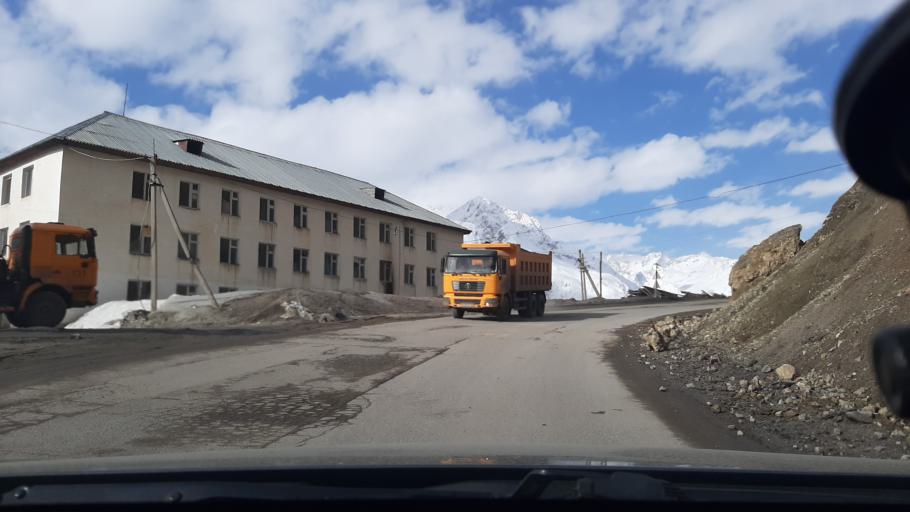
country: TJ
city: Tagob
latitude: 39.0605
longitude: 68.7106
